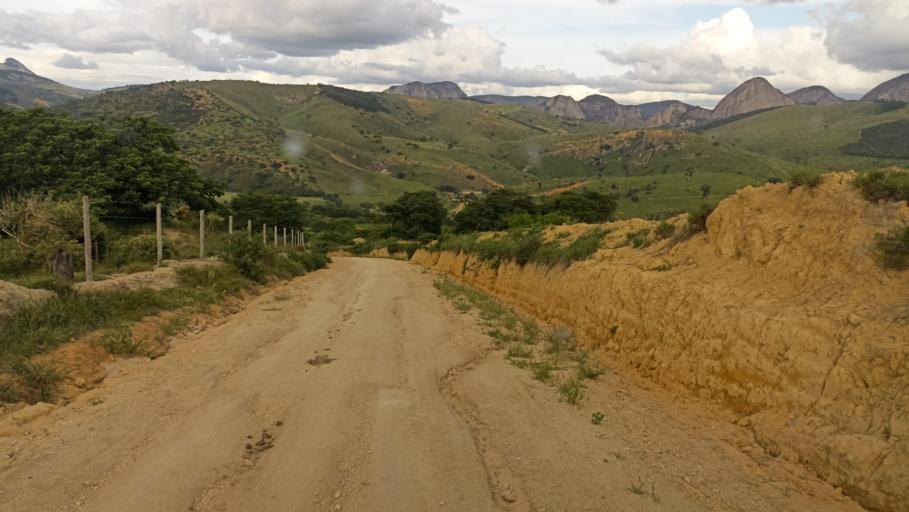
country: BR
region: Minas Gerais
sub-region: Almenara
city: Almenara
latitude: -16.5440
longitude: -40.4484
